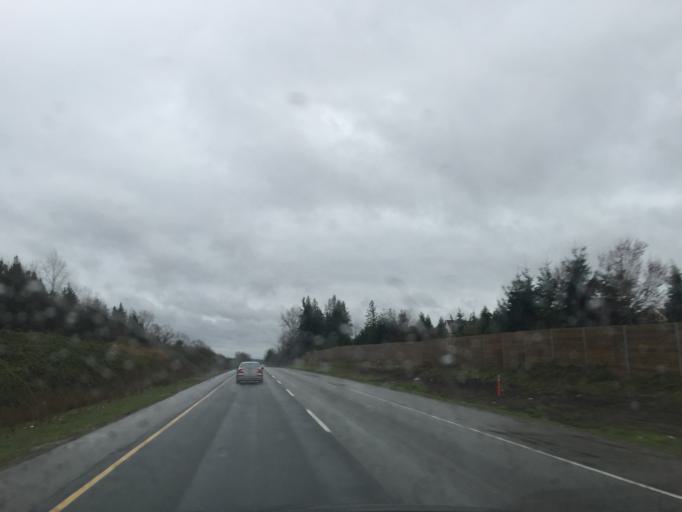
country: CA
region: British Columbia
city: Walnut Grove
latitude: 49.1552
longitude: -122.6359
